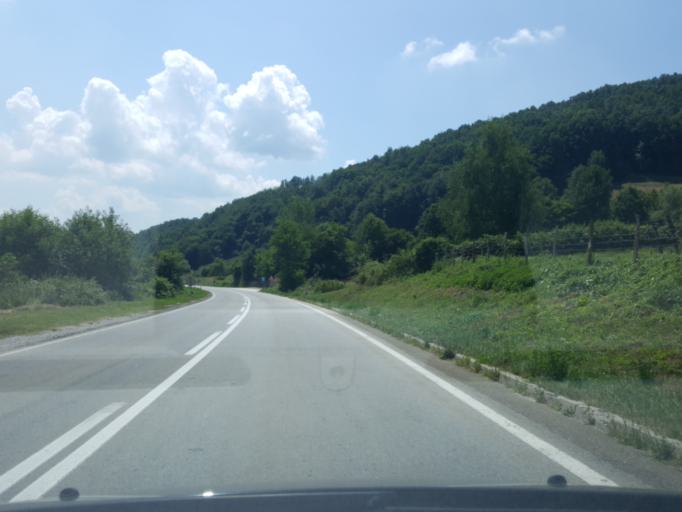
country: RS
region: Central Serbia
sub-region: Moravicki Okrug
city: Gornji Milanovac
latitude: 44.0855
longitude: 20.4798
